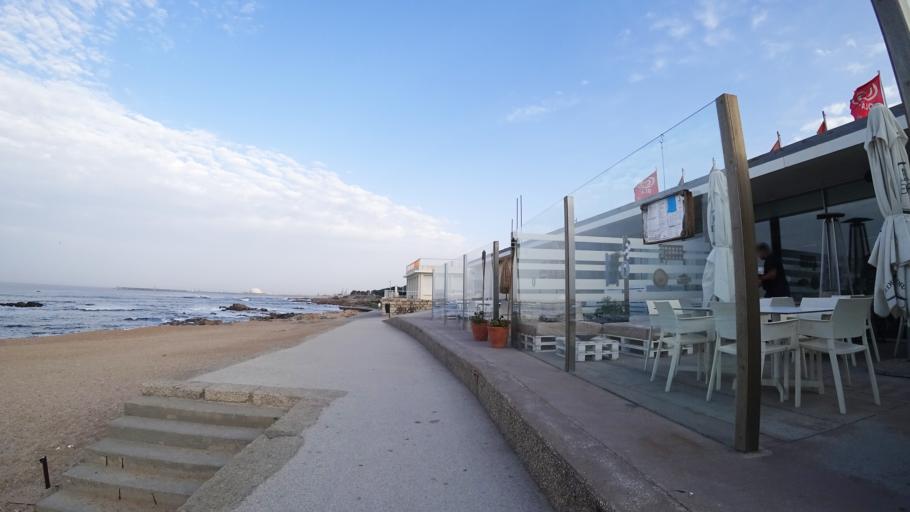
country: PT
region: Porto
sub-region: Matosinhos
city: Matosinhos
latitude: 41.1603
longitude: -8.6853
